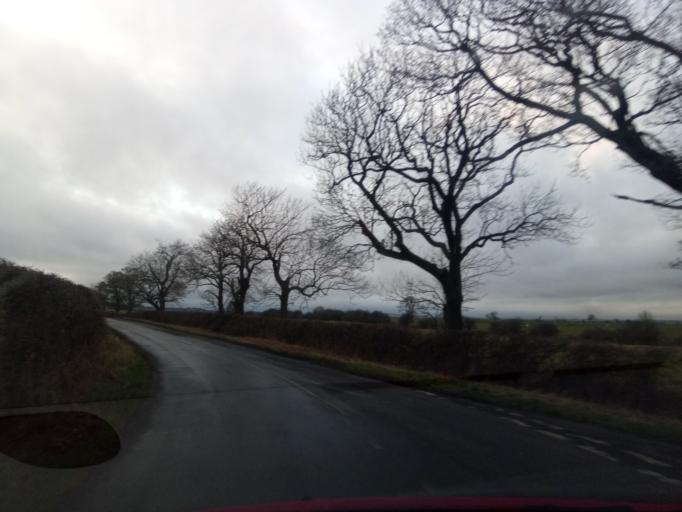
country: GB
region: England
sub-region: Northumberland
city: Meldon
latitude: 55.1430
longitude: -1.8159
